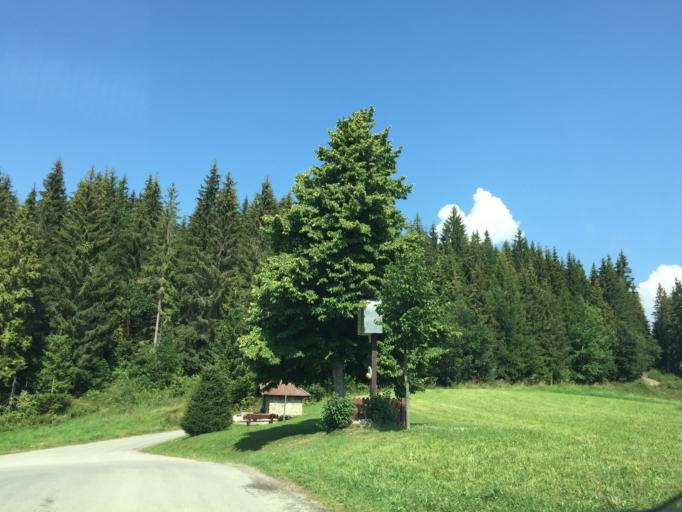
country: SK
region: Zilinsky
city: Oravska Lesna
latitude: 49.4325
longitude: 19.2978
